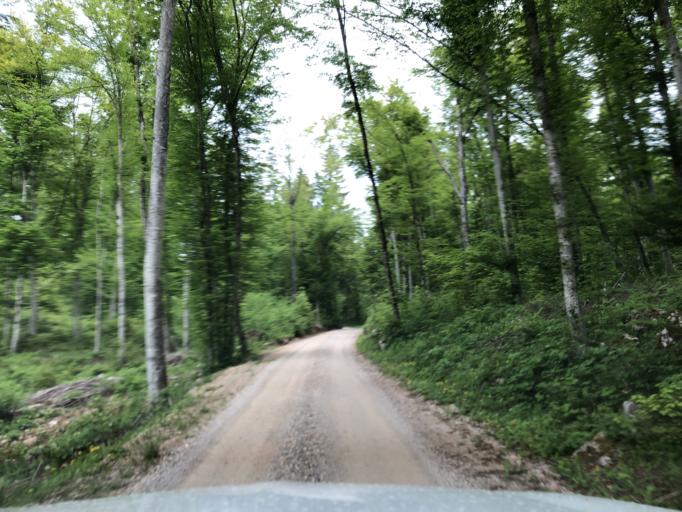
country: SI
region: Bloke
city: Nova Vas
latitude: 45.7477
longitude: 14.4661
